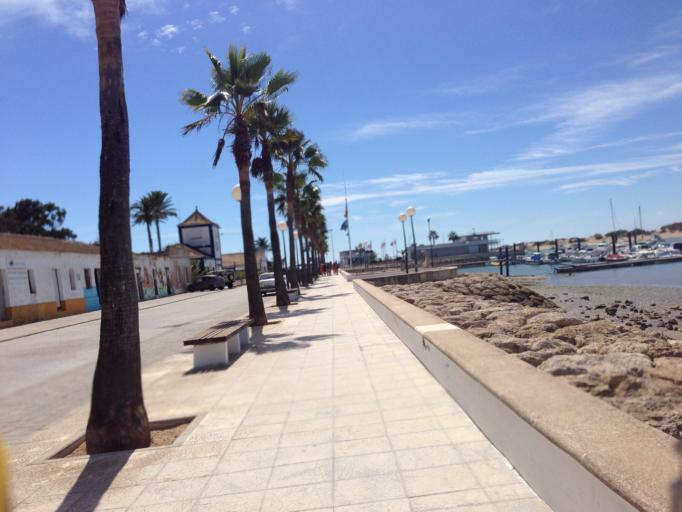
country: ES
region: Andalusia
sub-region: Provincia de Cadiz
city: Chiclana de la Frontera
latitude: 36.3964
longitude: -6.2072
